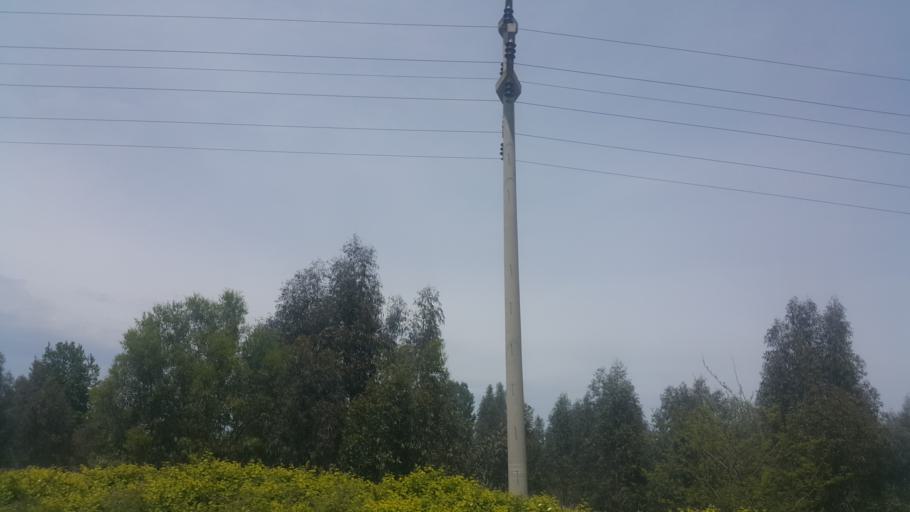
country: TR
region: Adana
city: Kosreli
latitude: 37.0678
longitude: 35.9892
